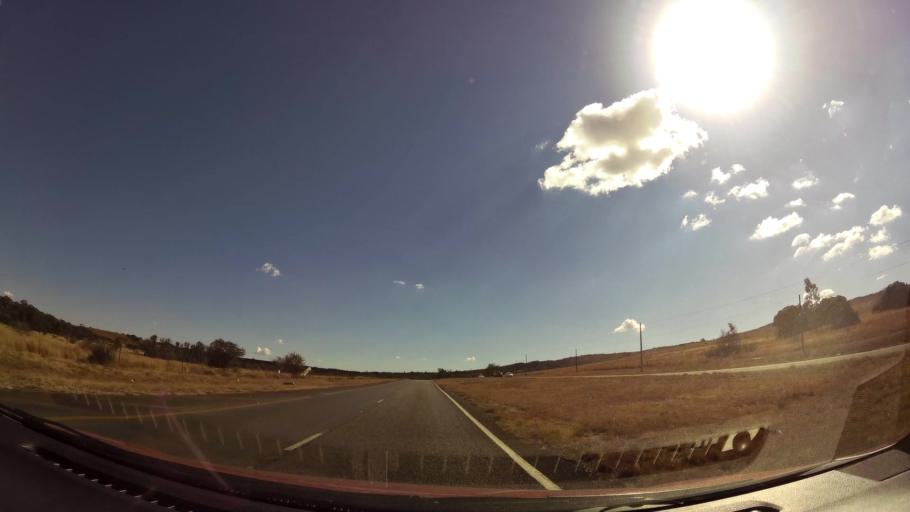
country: ZA
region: North-West
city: Fochville
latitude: -26.4350
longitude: 27.4763
